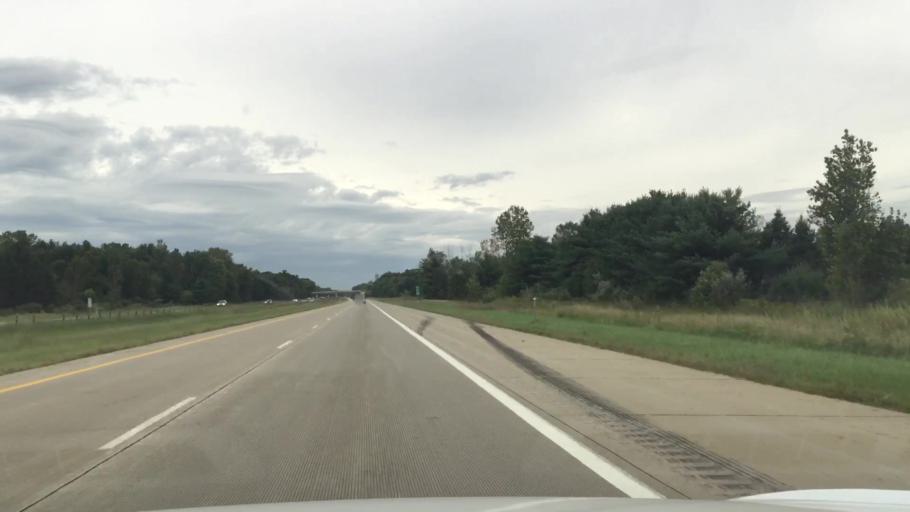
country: US
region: Michigan
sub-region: Saint Clair County
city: Saint Clair
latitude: 42.8420
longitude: -82.5867
